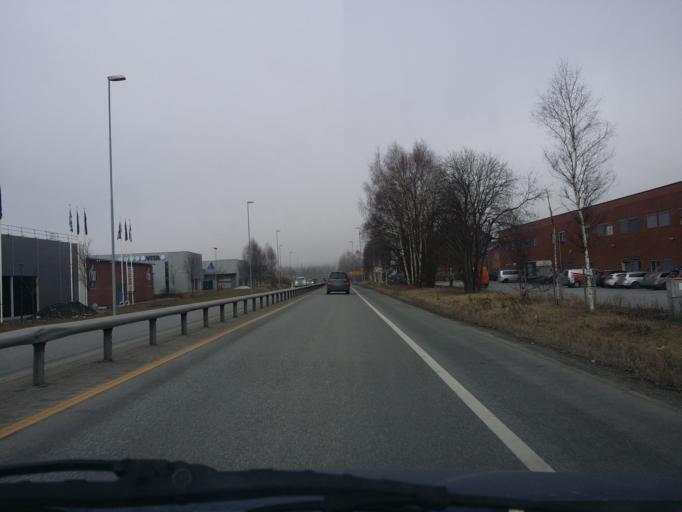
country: NO
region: Buskerud
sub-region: Nedre Eiker
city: Mjondalen
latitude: 59.7490
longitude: 10.0326
